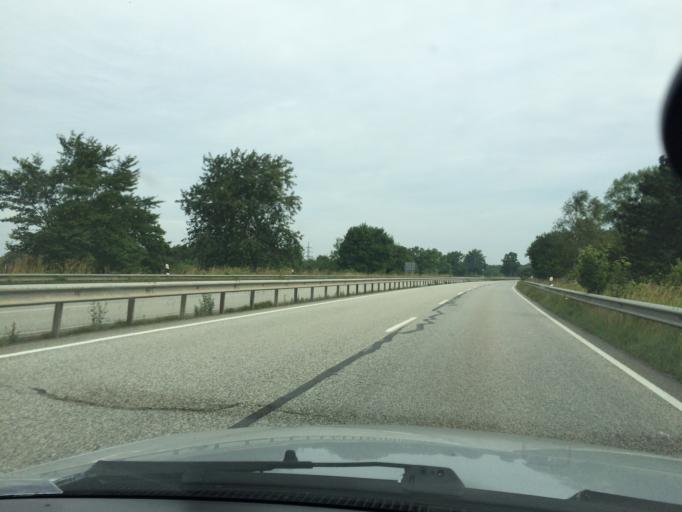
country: DE
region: Schleswig-Holstein
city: Harrislee
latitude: 54.7808
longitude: 9.4059
